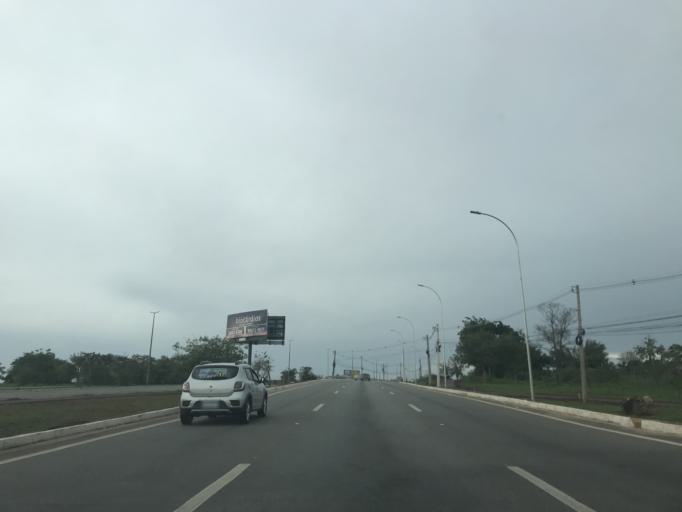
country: BR
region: Federal District
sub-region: Brasilia
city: Brasilia
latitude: -15.7222
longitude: -47.8963
